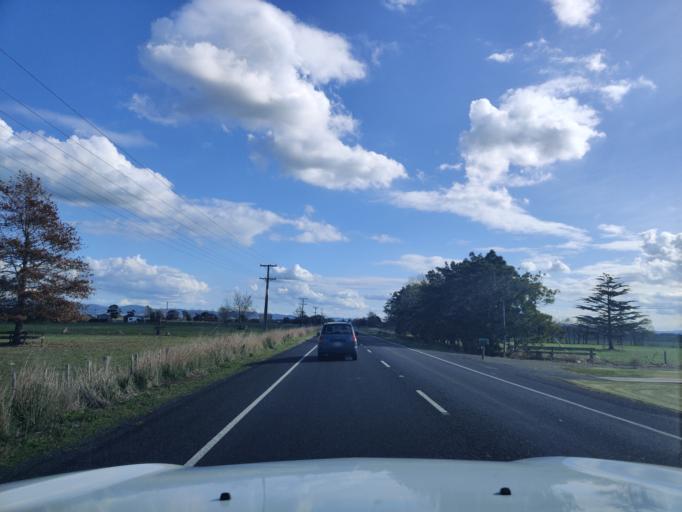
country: NZ
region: Waikato
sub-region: Hauraki District
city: Ngatea
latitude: -37.2730
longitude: 175.5175
